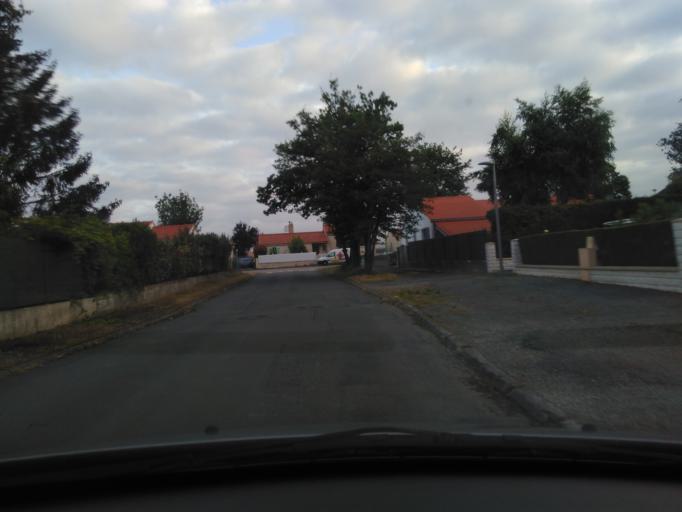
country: FR
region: Pays de la Loire
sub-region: Departement de la Vendee
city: Dompierre-sur-Yon
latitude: 46.7348
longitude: -1.3964
